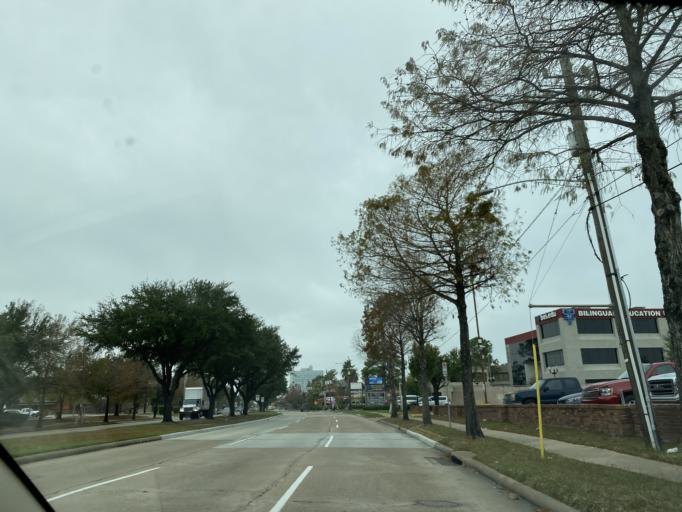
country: US
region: Texas
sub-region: Harris County
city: Bellaire
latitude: 29.7318
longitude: -95.4859
